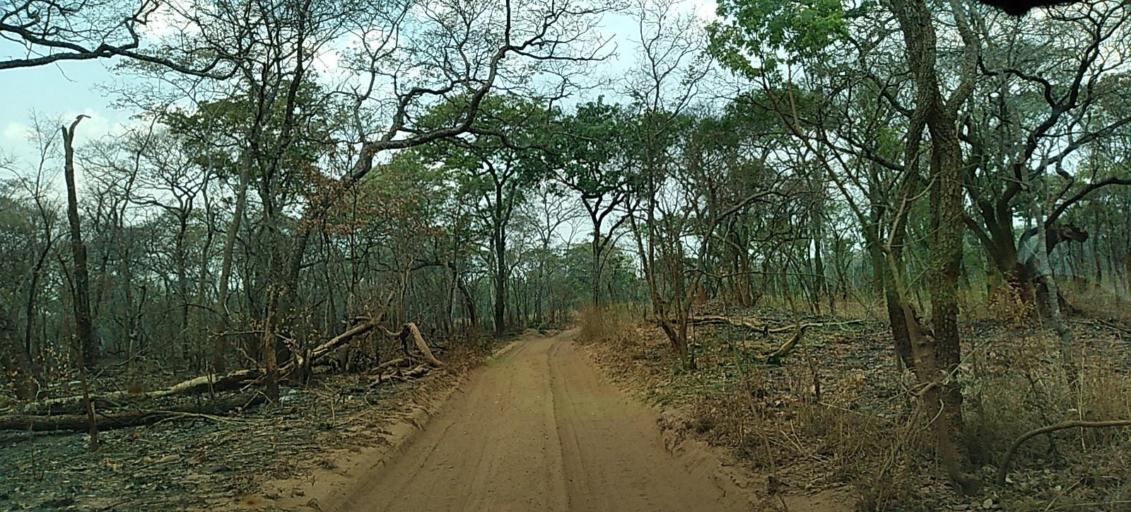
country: ZM
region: North-Western
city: Kabompo
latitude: -13.6098
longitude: 24.3805
